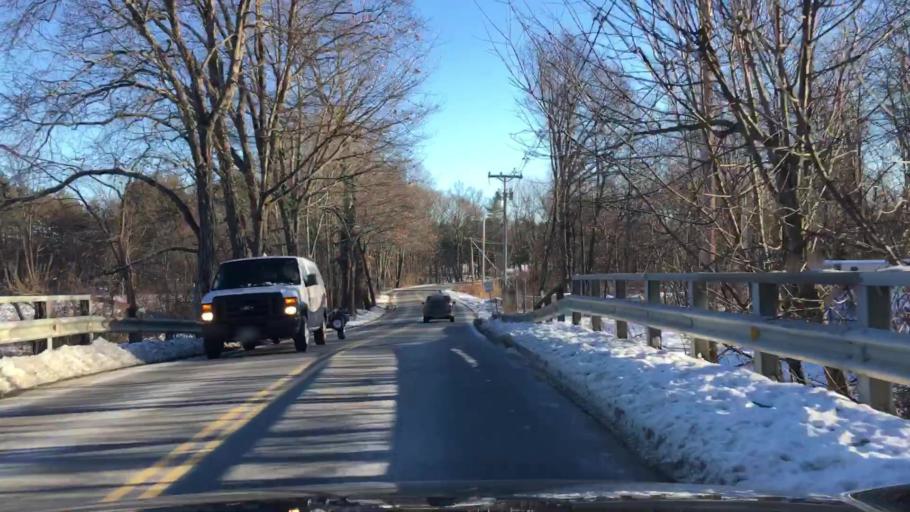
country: US
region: New Hampshire
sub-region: Hillsborough County
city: Milford
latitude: 42.8272
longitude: -71.5851
